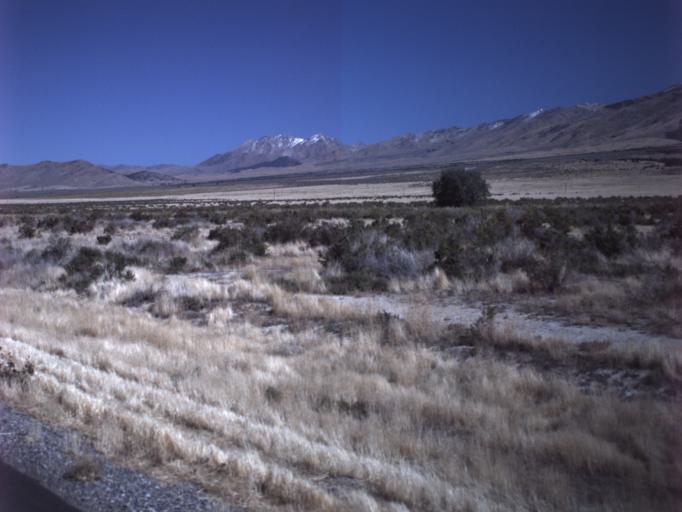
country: US
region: Utah
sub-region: Tooele County
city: Grantsville
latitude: 40.4708
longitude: -112.7464
